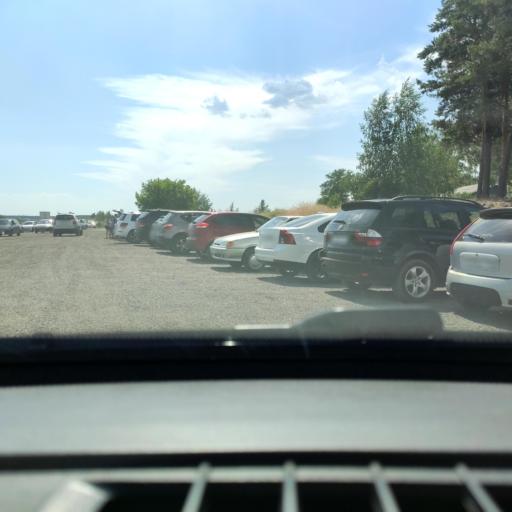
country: RU
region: Voronezj
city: Somovo
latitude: 51.7730
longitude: 39.3417
